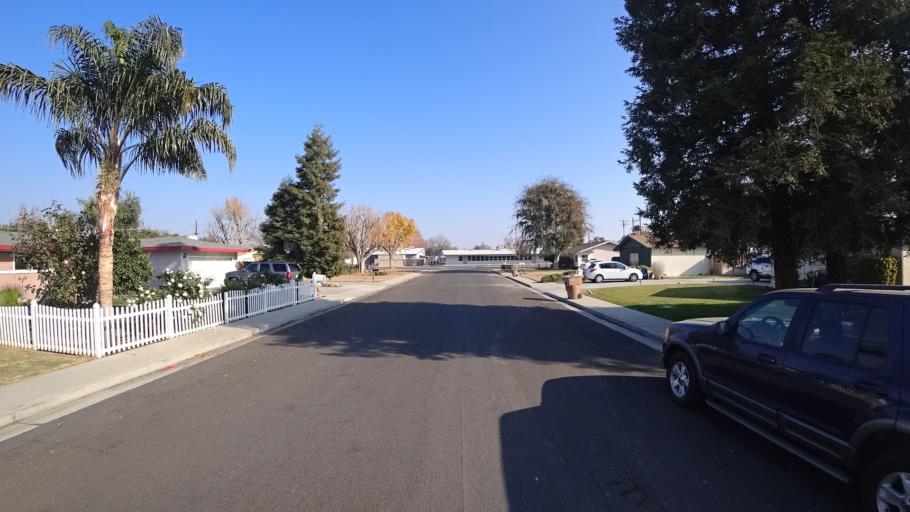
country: US
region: California
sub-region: Kern County
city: Bakersfield
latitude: 35.3436
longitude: -119.0472
